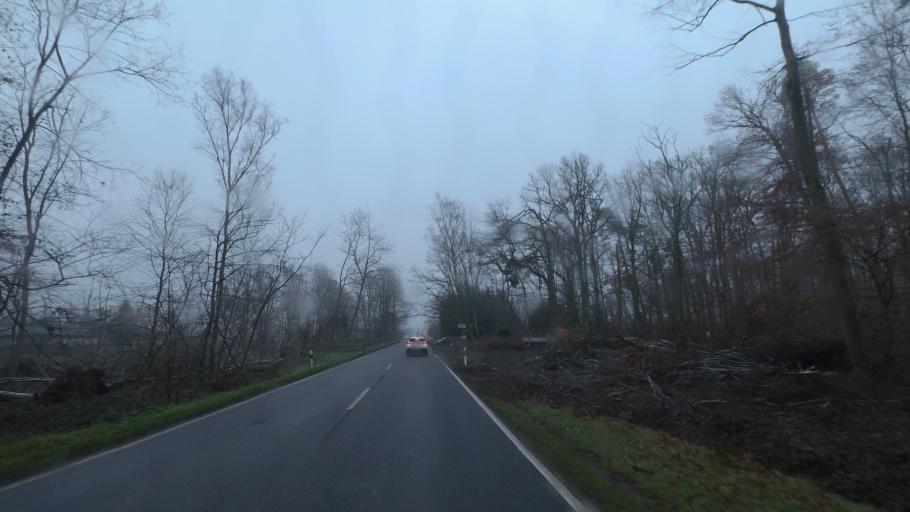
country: DE
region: Hesse
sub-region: Regierungsbezirk Darmstadt
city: Rodgau
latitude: 50.0555
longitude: 8.9214
